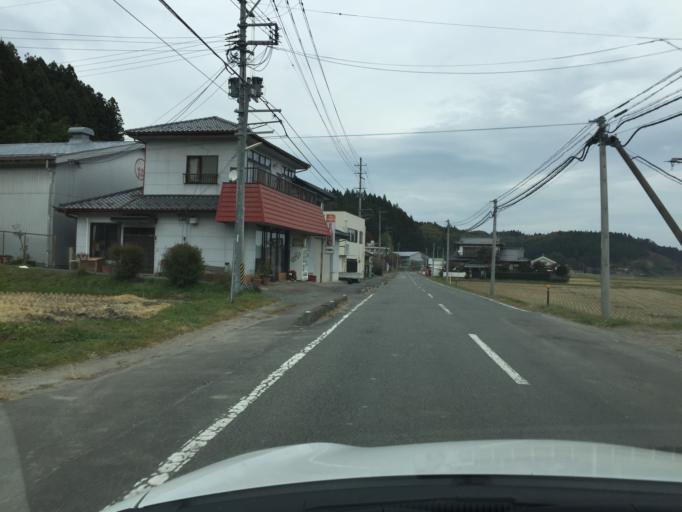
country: JP
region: Fukushima
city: Ishikawa
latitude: 37.1963
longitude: 140.6352
